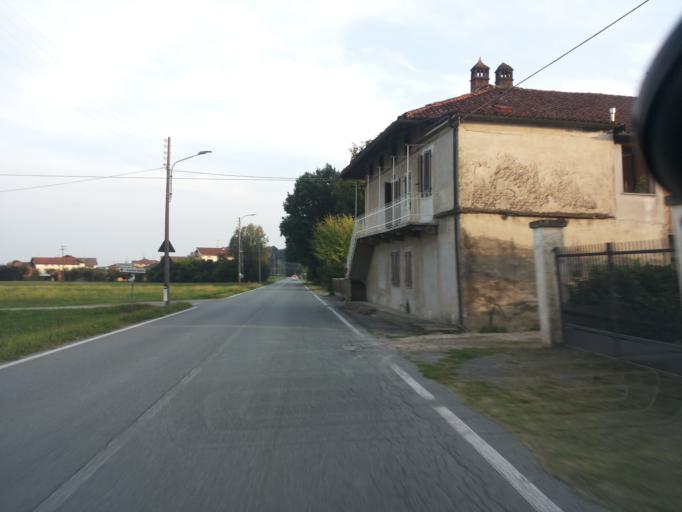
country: IT
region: Piedmont
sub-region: Provincia di Biella
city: Mottalciata
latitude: 45.5214
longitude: 8.1987
